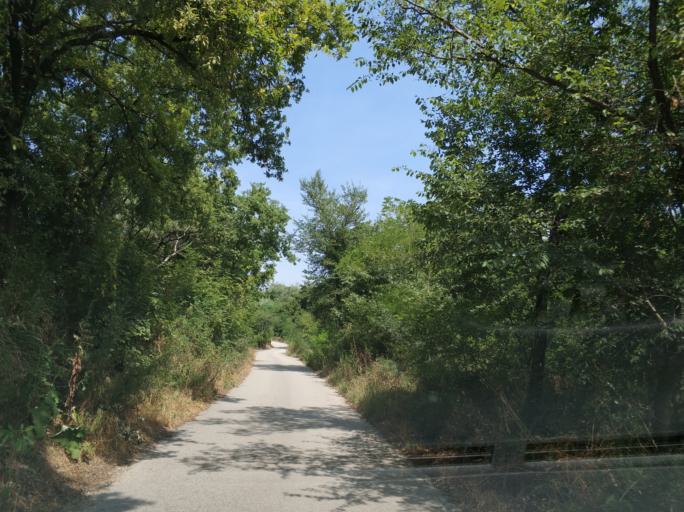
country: IT
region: Veneto
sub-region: Provincia di Padova
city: Arqua Petrarca
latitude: 45.2835
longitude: 11.7046
